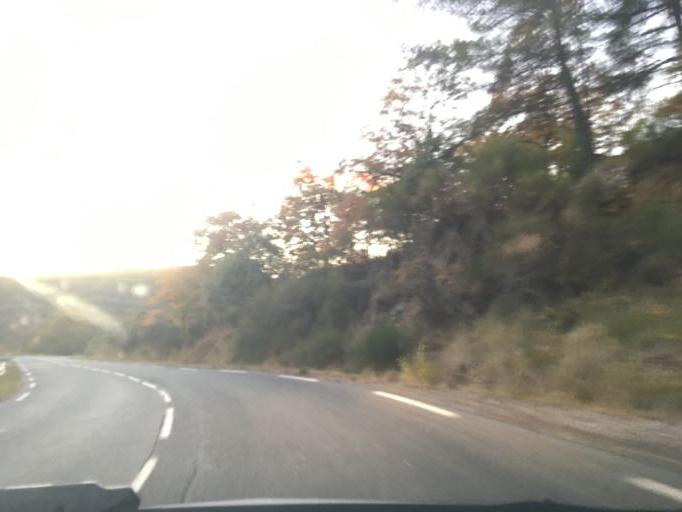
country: FR
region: Provence-Alpes-Cote d'Azur
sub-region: Departement du Var
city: Montferrat
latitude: 43.6286
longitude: 6.4885
